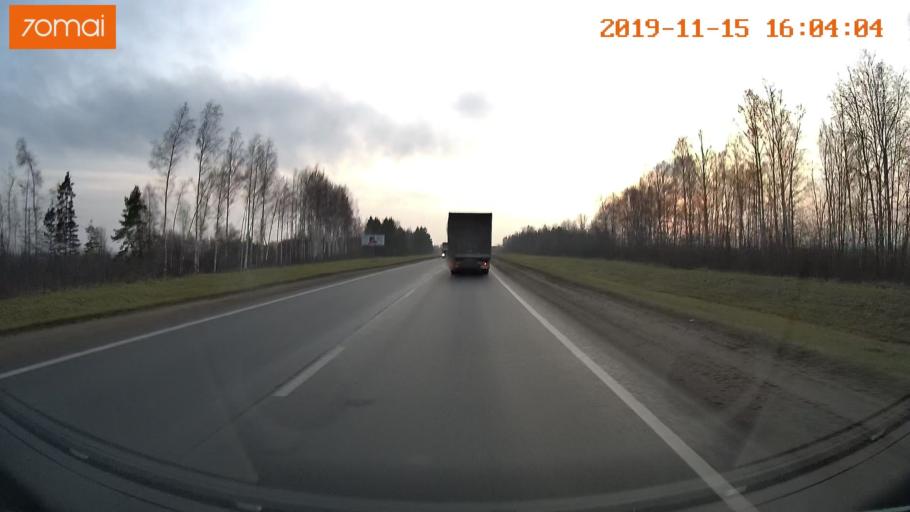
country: RU
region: Jaroslavl
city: Yaroslavl
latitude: 57.7517
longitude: 39.9065
